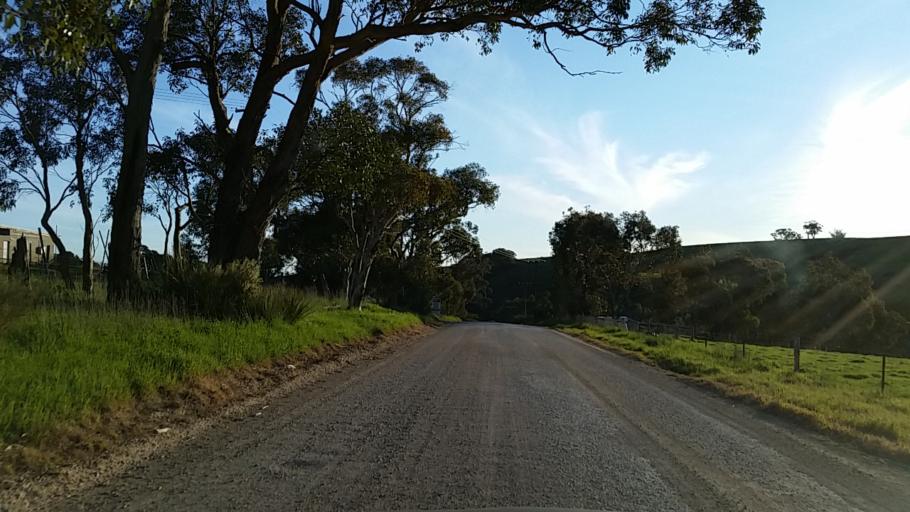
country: AU
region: South Australia
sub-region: Alexandrina
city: Mount Compass
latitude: -35.2854
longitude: 138.6942
